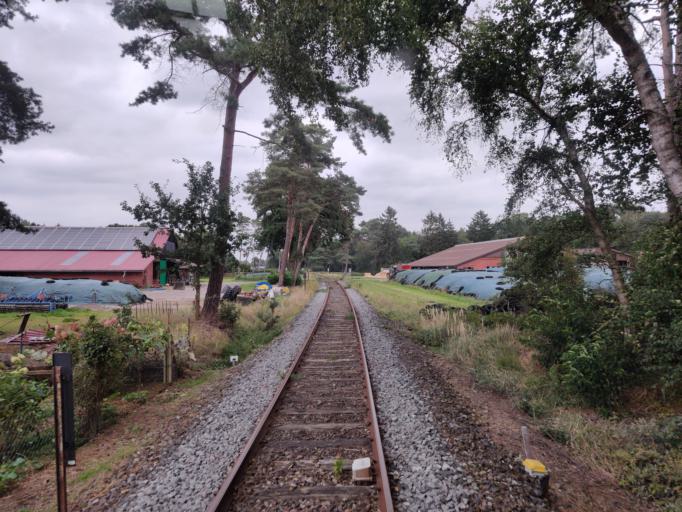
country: DE
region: Lower Saxony
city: Worpswede
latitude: 53.2451
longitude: 8.9591
